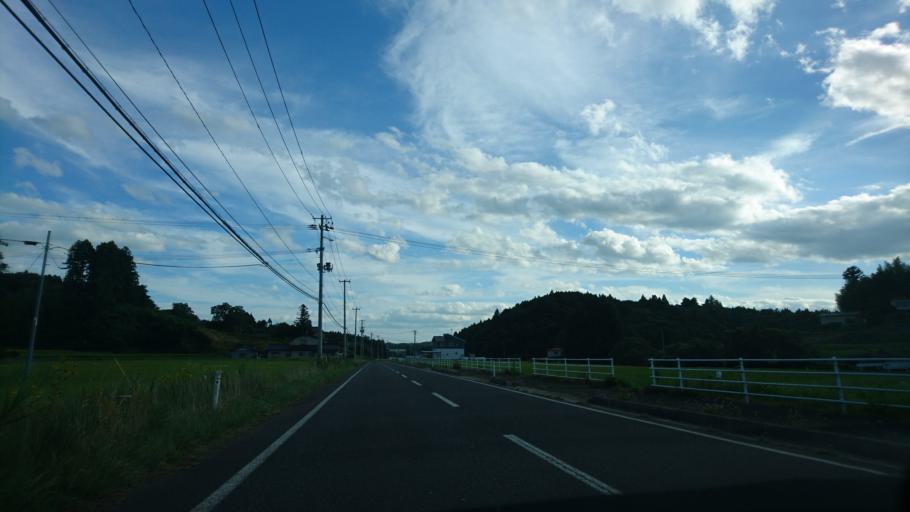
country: JP
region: Iwate
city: Ichinoseki
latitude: 38.8582
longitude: 141.1842
